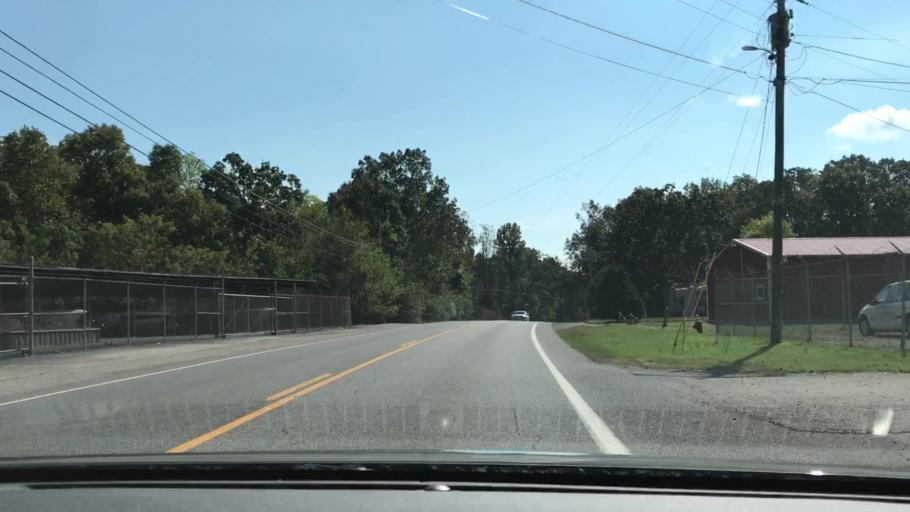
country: US
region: Kentucky
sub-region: Marshall County
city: Benton
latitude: 36.7747
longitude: -88.1413
